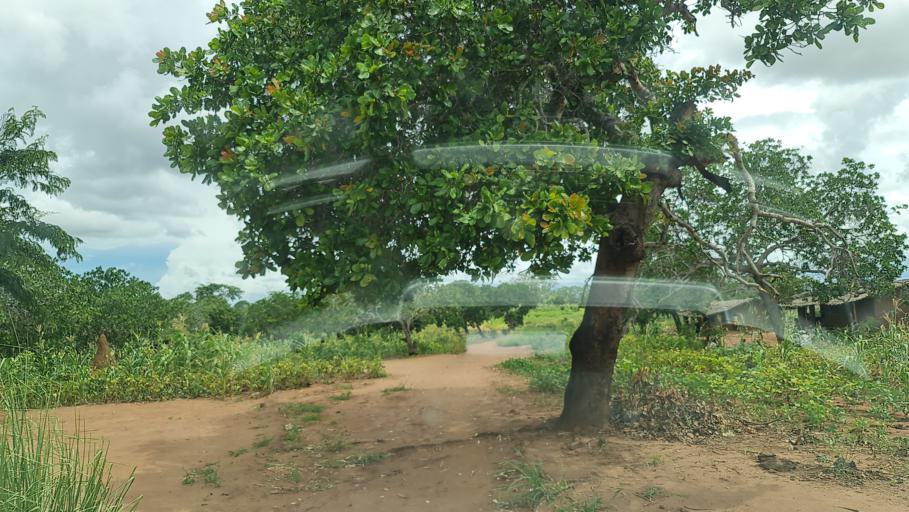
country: MZ
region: Nampula
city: Nacala
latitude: -14.7808
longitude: 39.9960
